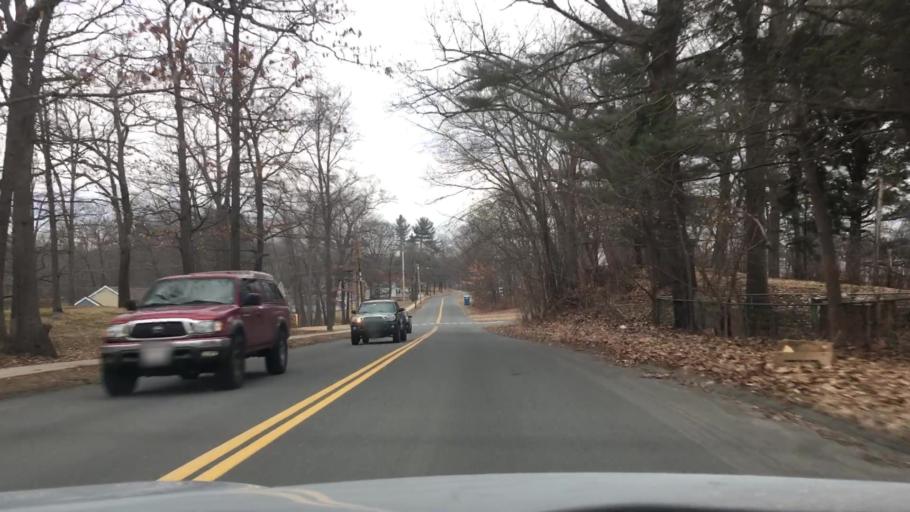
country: US
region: Massachusetts
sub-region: Franklin County
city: Greenfield
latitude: 42.6006
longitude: -72.6110
